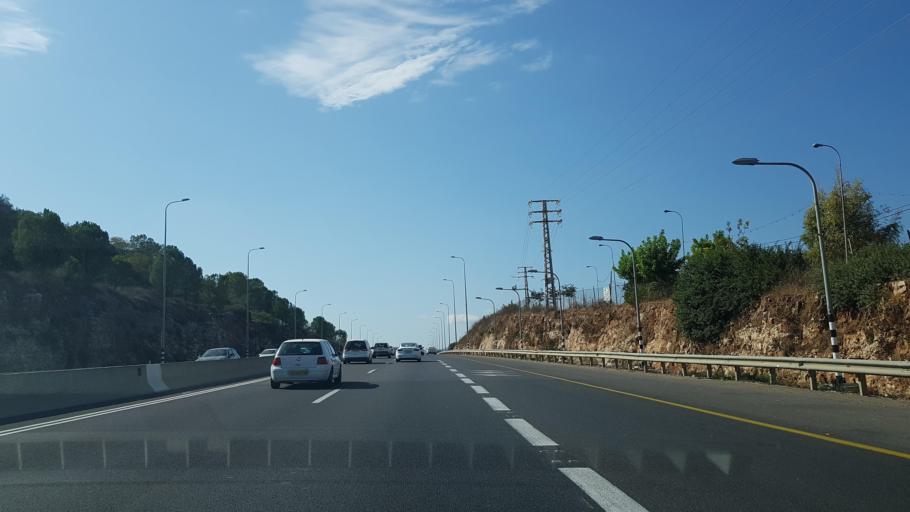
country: IL
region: Northern District
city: Rumat Heib
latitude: 32.7679
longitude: 35.3087
